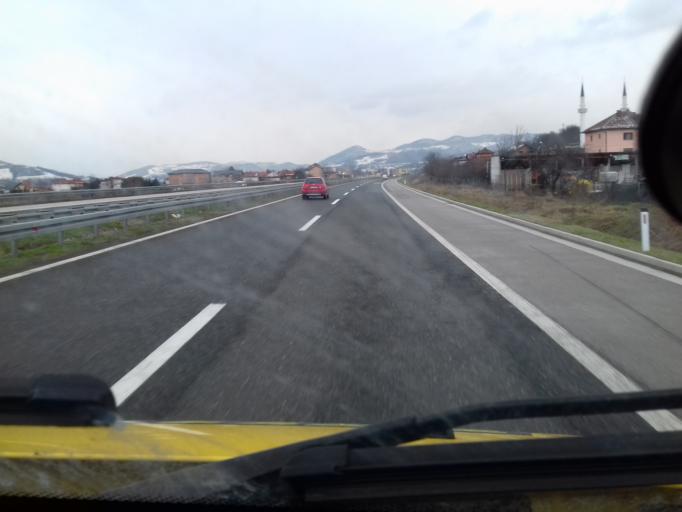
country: BA
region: Federation of Bosnia and Herzegovina
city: Gornje Mostre
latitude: 44.0269
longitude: 18.1313
